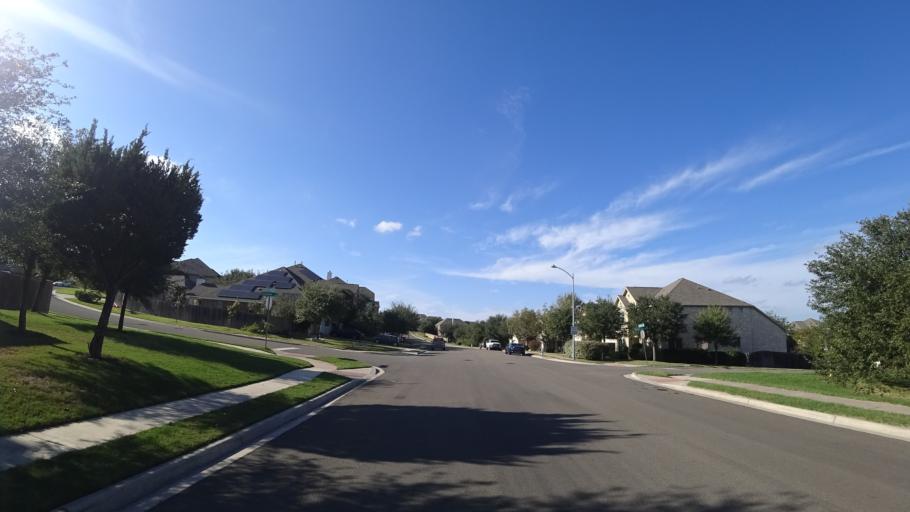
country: US
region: Texas
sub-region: Travis County
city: Barton Creek
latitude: 30.2473
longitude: -97.8731
